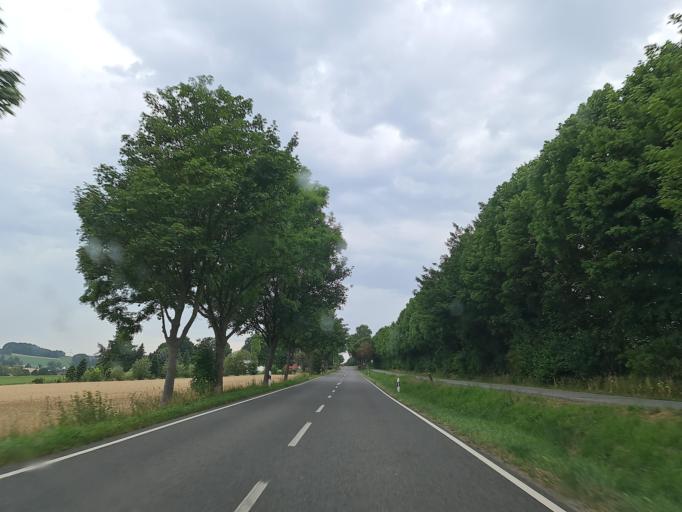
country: DE
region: Saxony
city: Eppendorf
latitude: 50.7940
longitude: 13.2490
